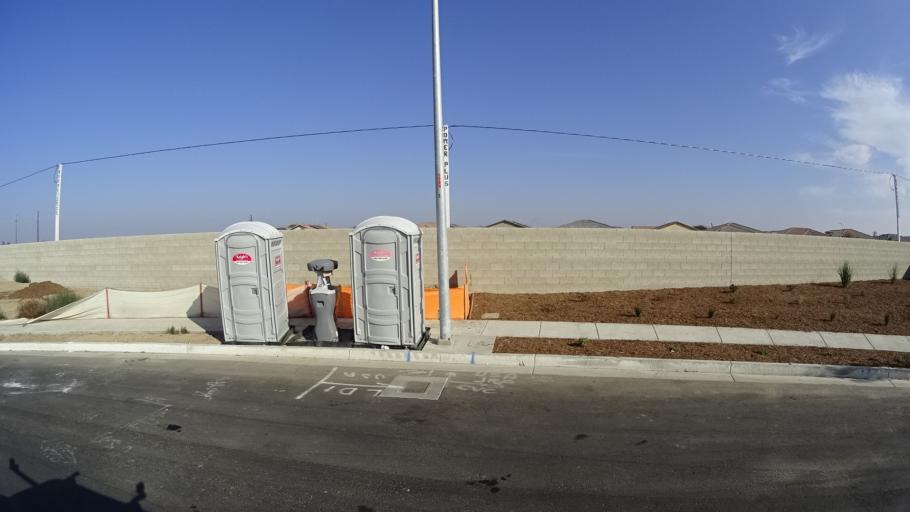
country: US
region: California
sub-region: Kern County
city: Rosedale
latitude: 35.3530
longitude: -119.1741
